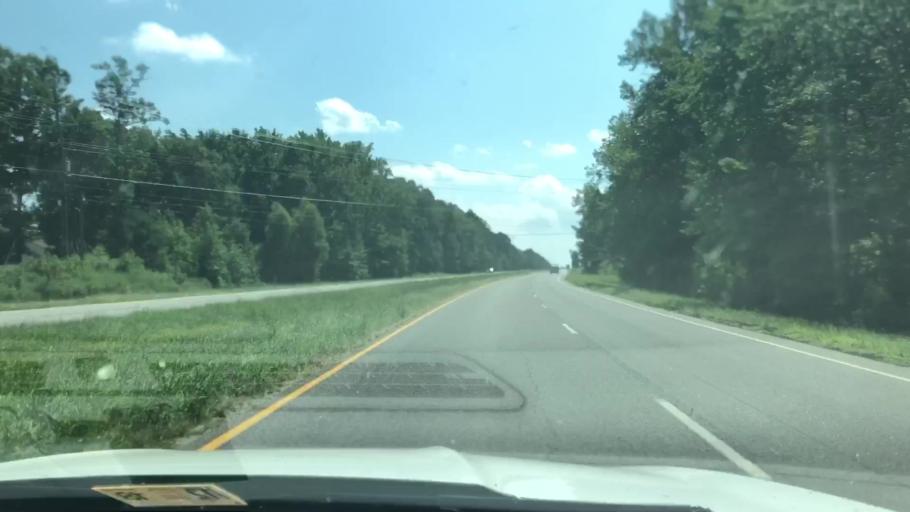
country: US
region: Virginia
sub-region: Essex County
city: Tappahannock
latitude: 37.8462
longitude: -76.8043
